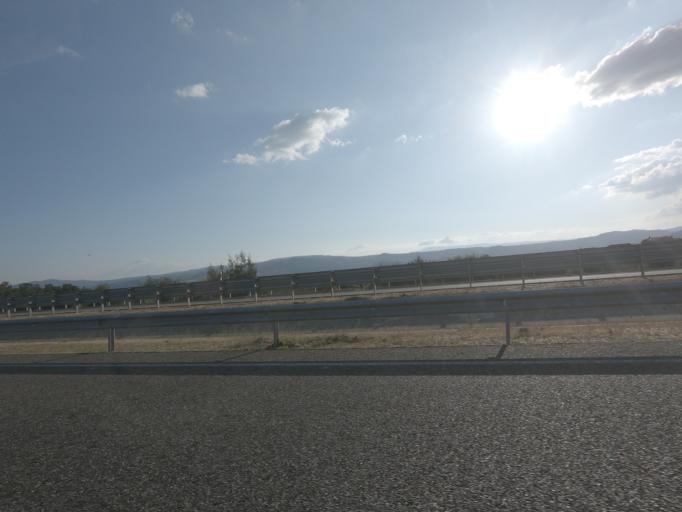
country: ES
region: Galicia
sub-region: Provincia de Ourense
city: Verin
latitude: 41.8958
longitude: -7.4242
